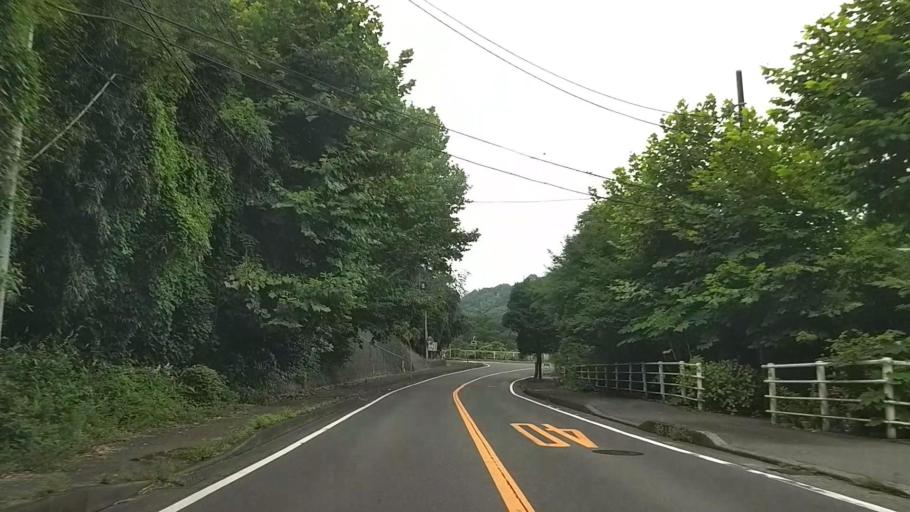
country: JP
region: Kanagawa
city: Hadano
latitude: 35.3389
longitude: 139.2224
